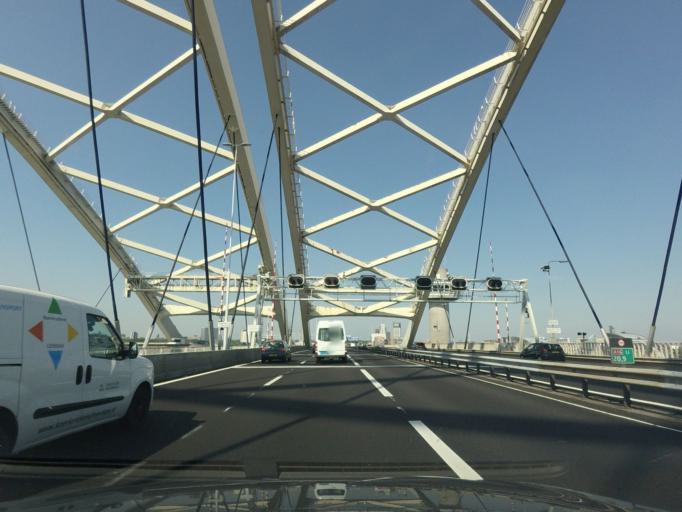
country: NL
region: South Holland
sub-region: Gemeente Rotterdam
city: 's-Gravenland
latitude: 51.9039
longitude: 4.5431
